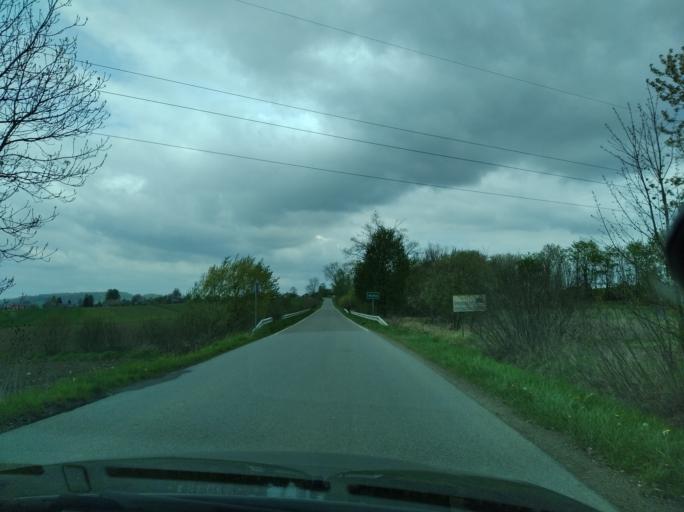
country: PL
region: Subcarpathian Voivodeship
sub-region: Powiat brzozowski
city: Turze Pole
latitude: 49.6342
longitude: 22.0056
